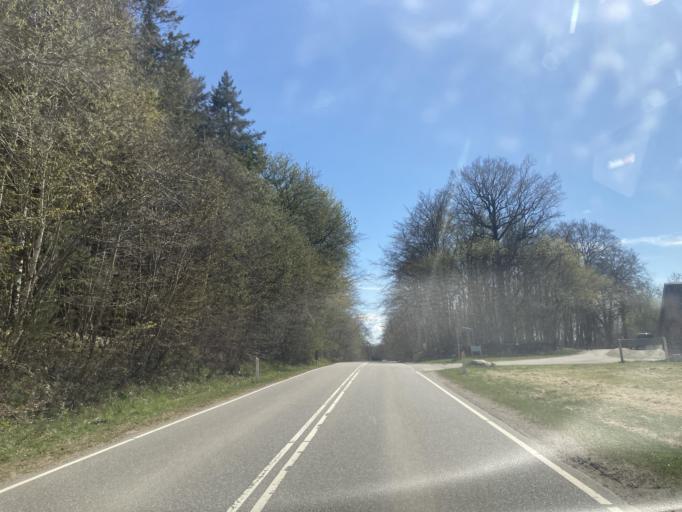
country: DK
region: Capital Region
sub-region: Gribskov Kommune
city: Graested
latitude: 56.0095
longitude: 12.2625
